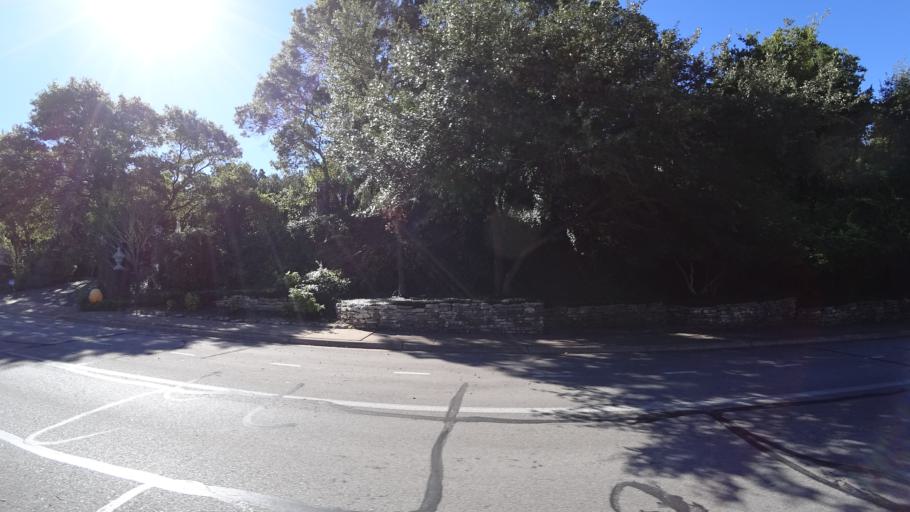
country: US
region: Texas
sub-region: Travis County
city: West Lake Hills
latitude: 30.3607
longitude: -97.7736
